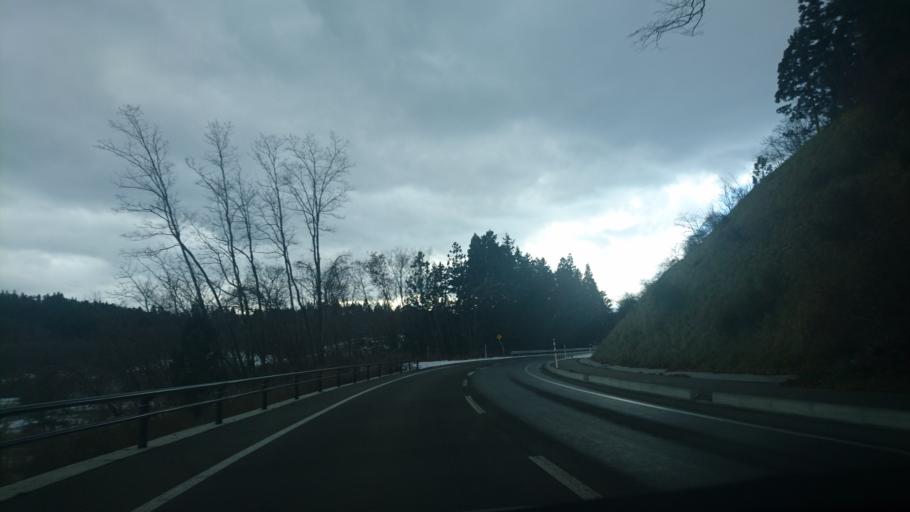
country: JP
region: Iwate
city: Mizusawa
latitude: 39.1557
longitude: 141.2400
